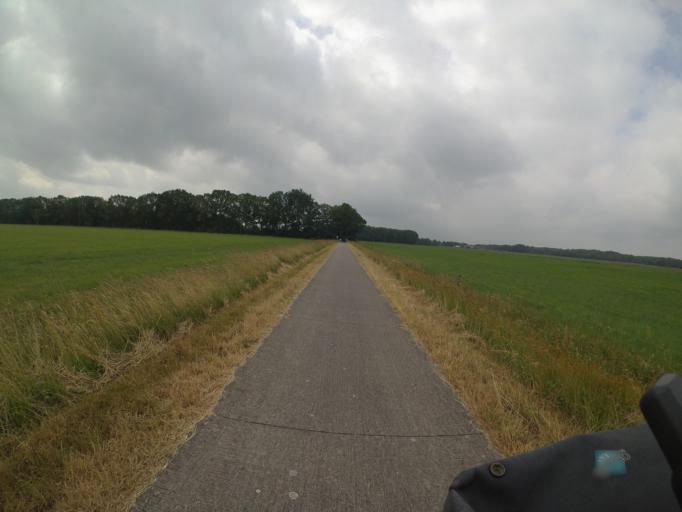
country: NL
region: Drenthe
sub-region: Gemeente Westerveld
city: Havelte
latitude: 52.8405
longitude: 6.2816
